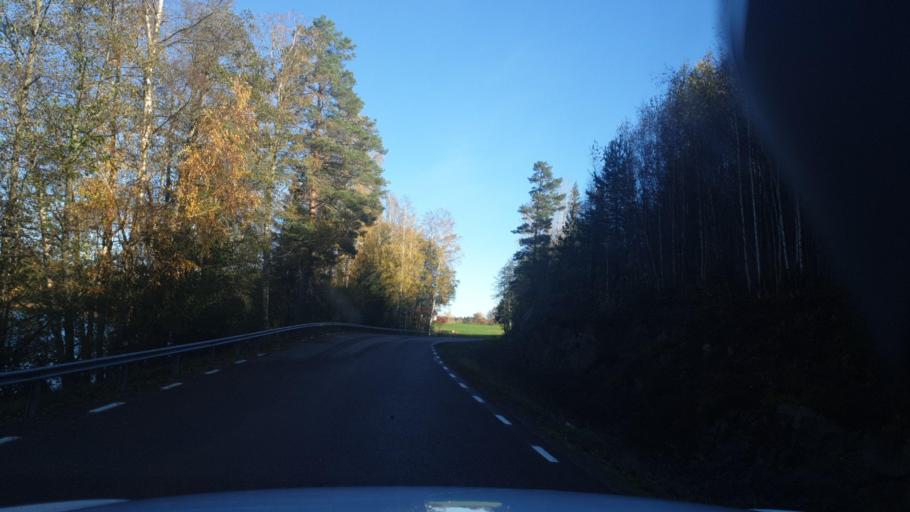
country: SE
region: Vaermland
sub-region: Arvika Kommun
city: Arvika
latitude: 59.5907
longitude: 12.7520
